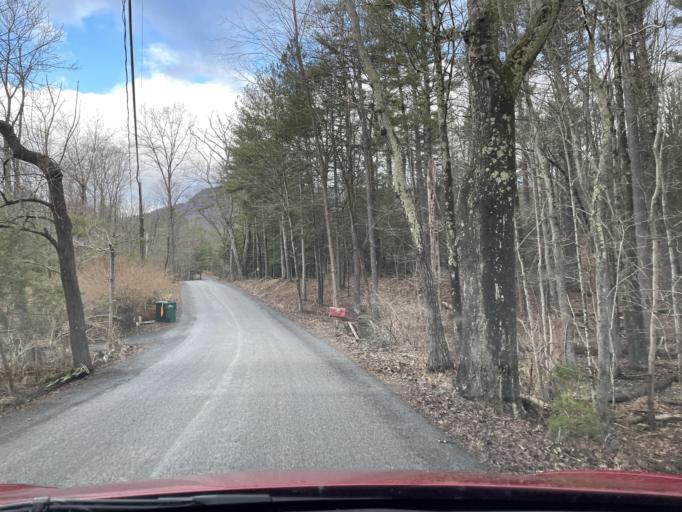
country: US
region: New York
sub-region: Ulster County
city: Manorville
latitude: 42.0804
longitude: -74.0514
